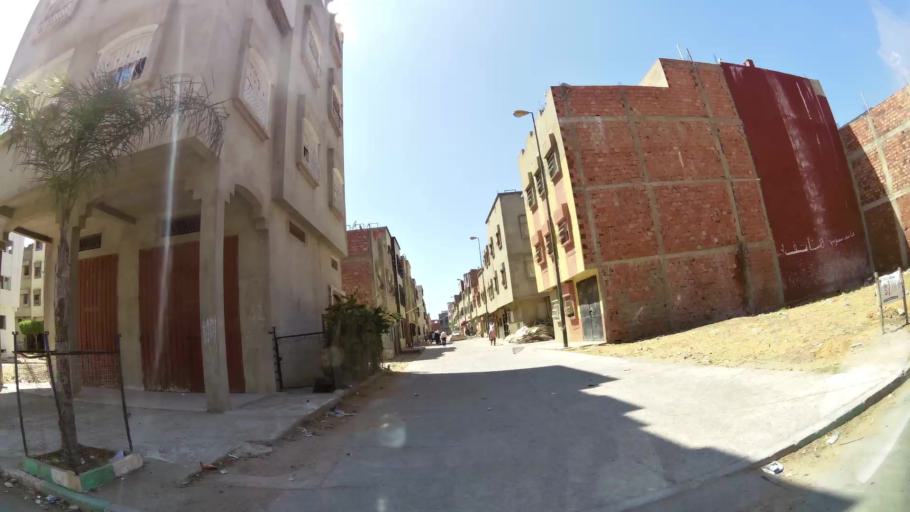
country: MA
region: Gharb-Chrarda-Beni Hssen
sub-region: Kenitra Province
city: Kenitra
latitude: 34.2434
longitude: -6.5388
